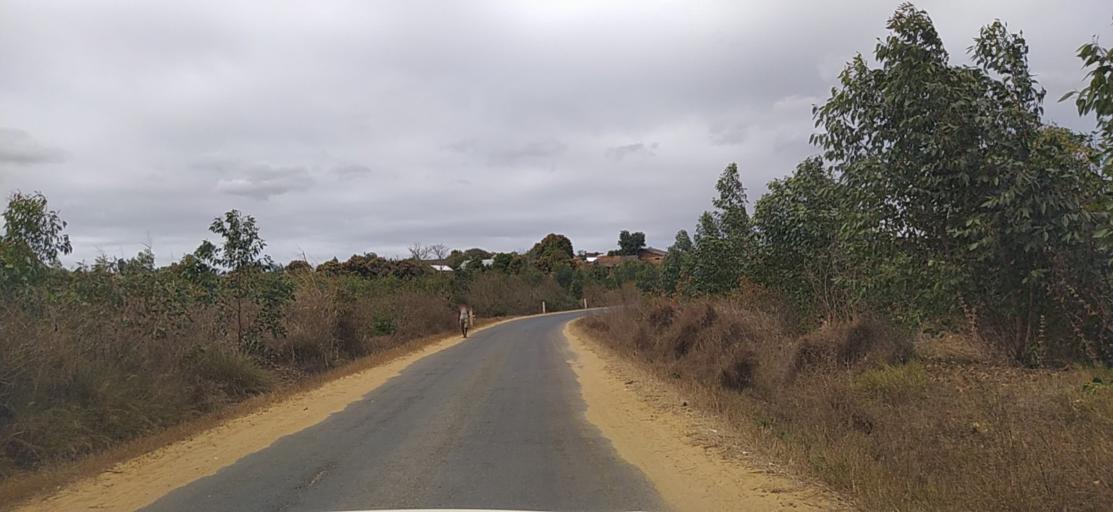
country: MG
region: Alaotra Mangoro
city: Ambatondrazaka
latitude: -17.9306
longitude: 48.2544
